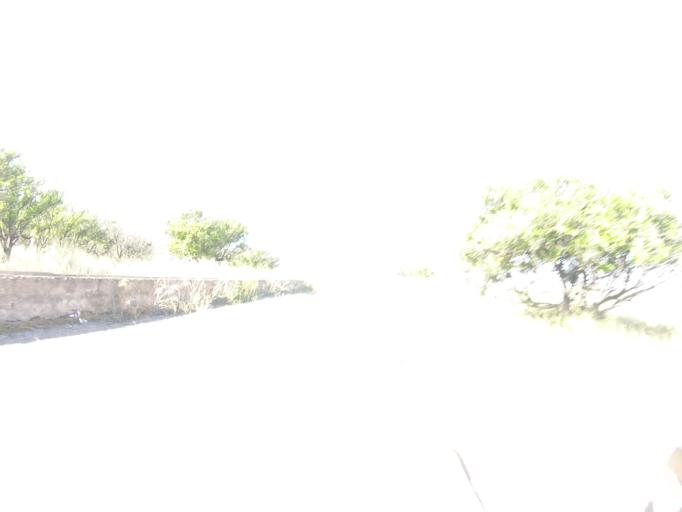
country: ES
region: Valencia
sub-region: Provincia de Castello
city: Torreblanca
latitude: 40.2102
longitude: 0.2280
